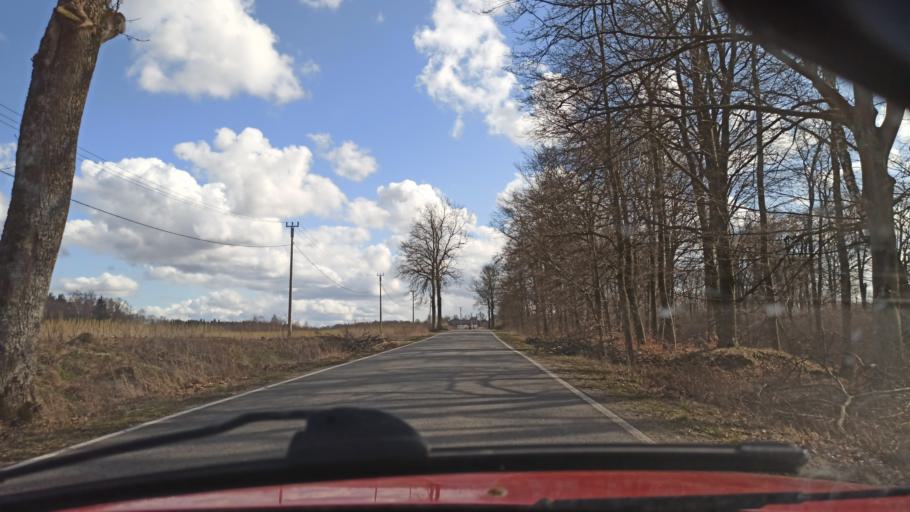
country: PL
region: Warmian-Masurian Voivodeship
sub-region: Powiat elblaski
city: Tolkmicko
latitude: 54.2754
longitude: 19.4836
